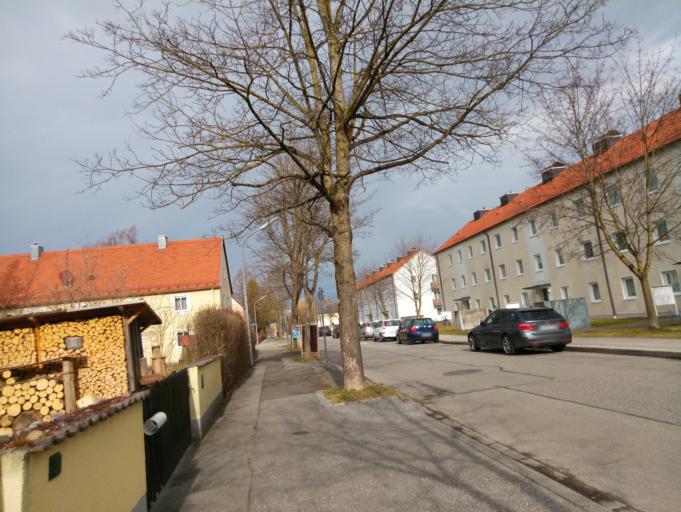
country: DE
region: Bavaria
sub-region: Upper Bavaria
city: Weilheim
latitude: 47.8446
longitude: 11.1537
